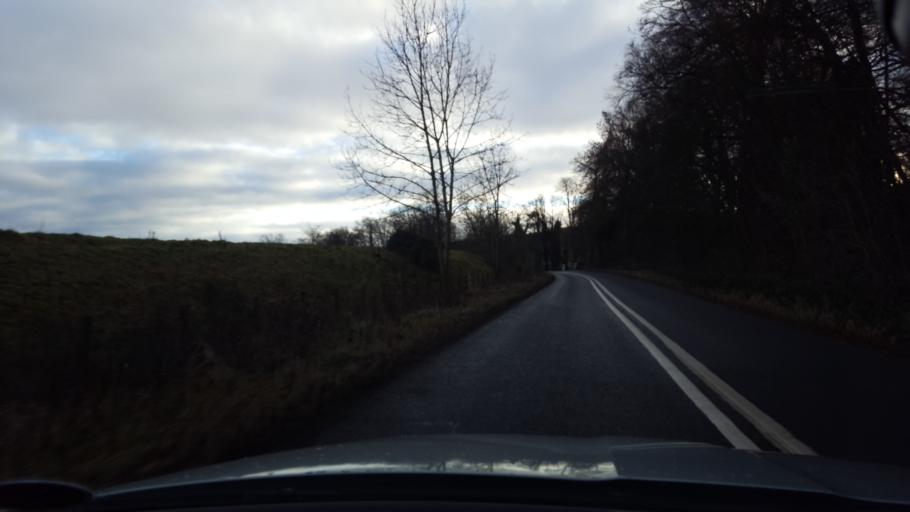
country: GB
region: Scotland
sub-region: Perth and Kinross
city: Milnathort
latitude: 56.2669
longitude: -3.3845
